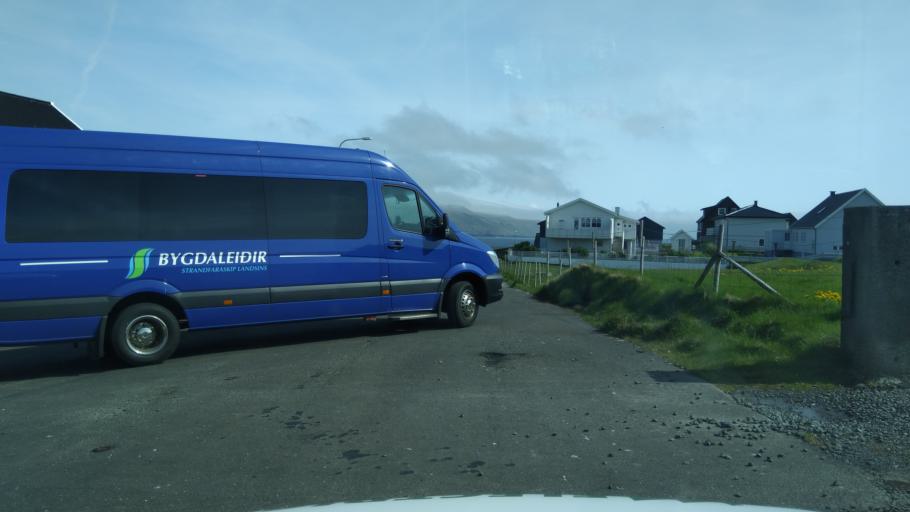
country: FO
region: Sandoy
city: Sandur
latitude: 61.8335
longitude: -6.8192
